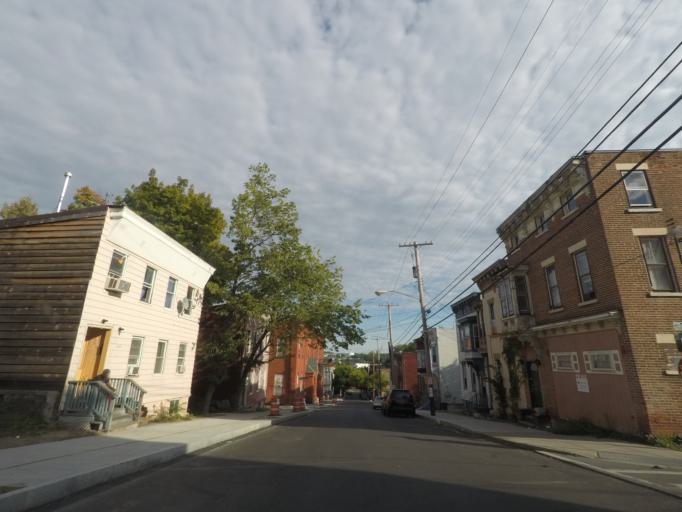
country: US
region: New York
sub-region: Albany County
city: Albany
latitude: 42.6383
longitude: -73.7630
